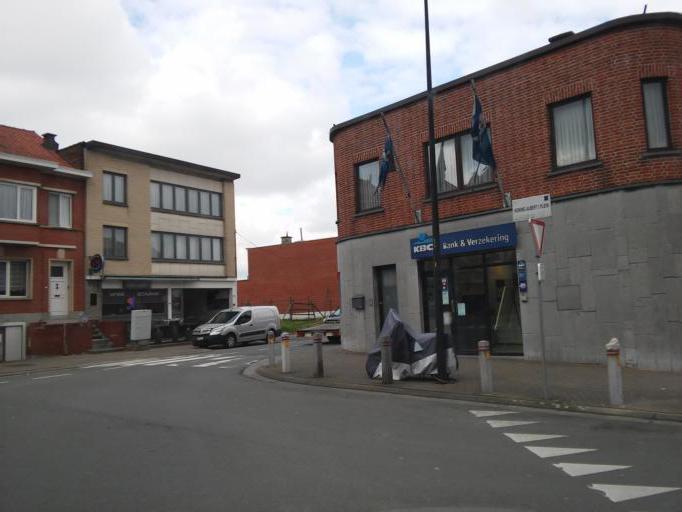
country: BE
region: Flanders
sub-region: Provincie Vlaams-Brabant
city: Drogenbos
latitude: 50.8056
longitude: 4.2844
